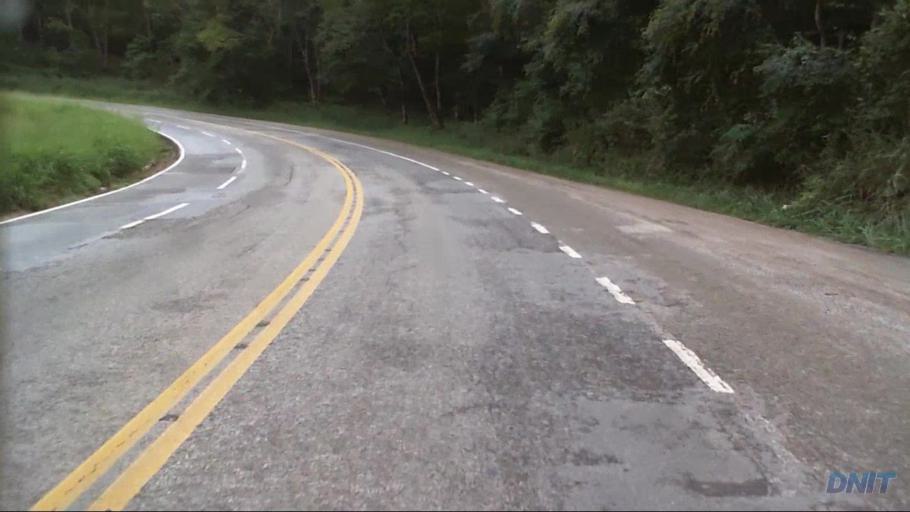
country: BR
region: Minas Gerais
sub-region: Joao Monlevade
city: Joao Monlevade
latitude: -19.8393
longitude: -43.3220
